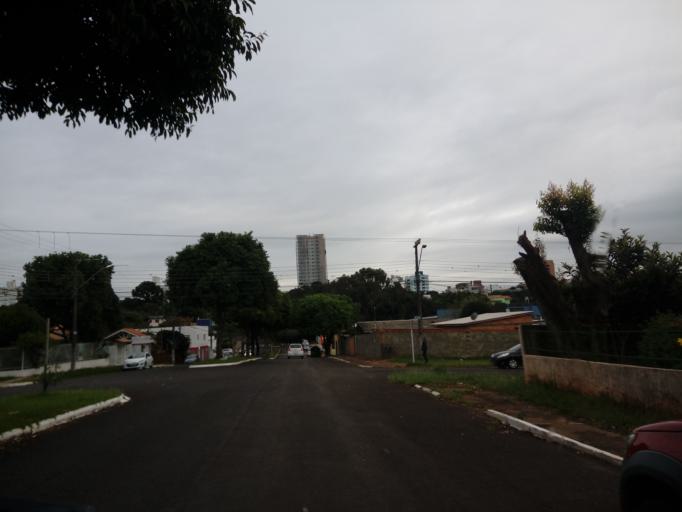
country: BR
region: Santa Catarina
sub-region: Chapeco
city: Chapeco
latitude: -27.0974
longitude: -52.6066
